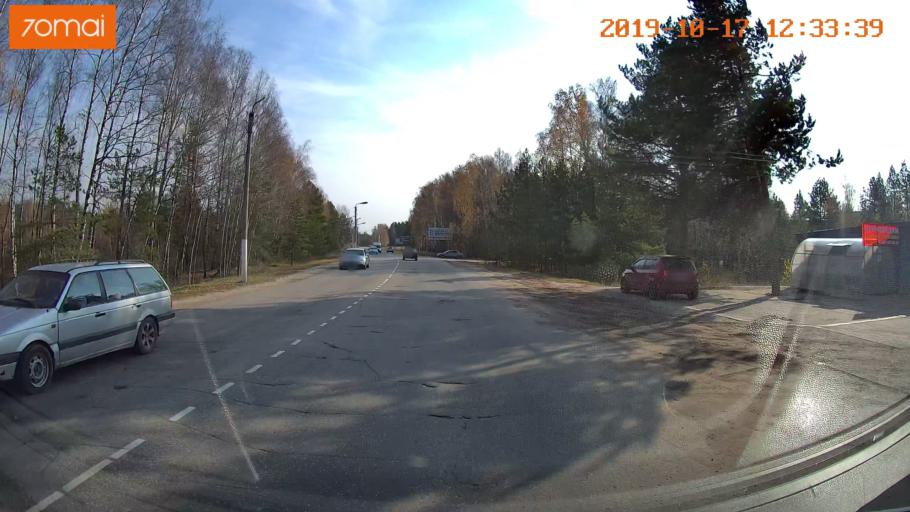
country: RU
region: Rjazan
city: Kasimov
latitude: 54.9530
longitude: 41.3557
